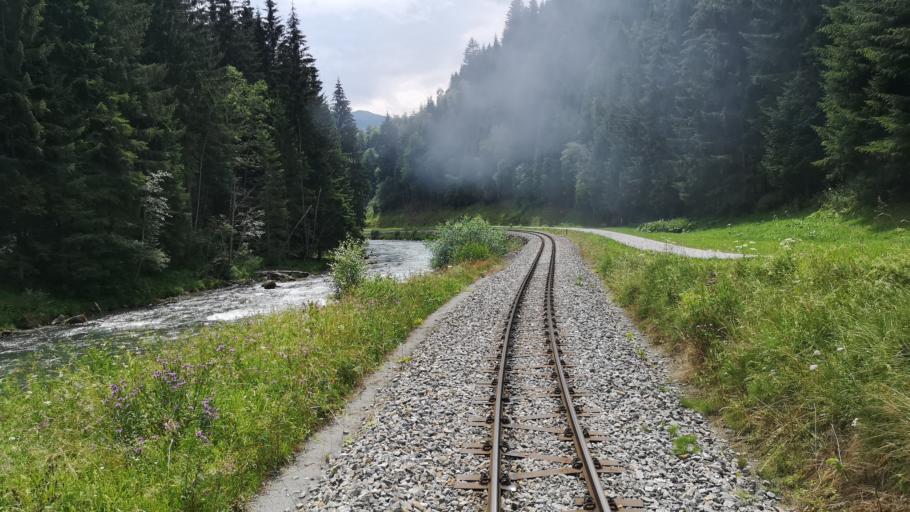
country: AT
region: Salzburg
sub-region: Politischer Bezirk Tamsweg
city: Ramingstein
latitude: 47.0948
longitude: 13.8207
